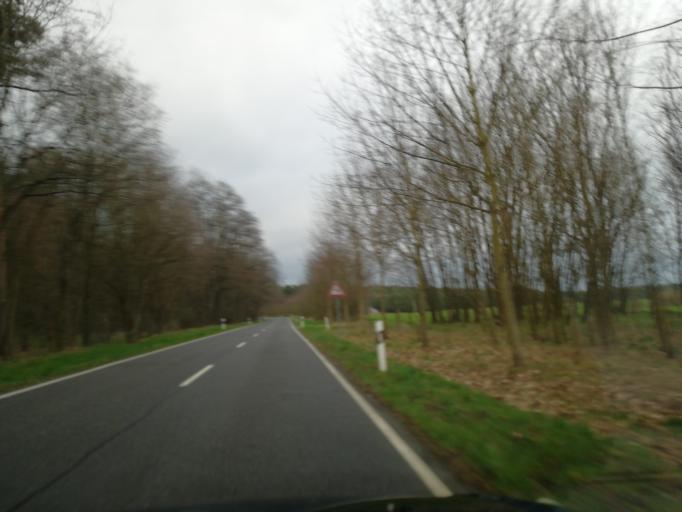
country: DE
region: Brandenburg
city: Vetschau
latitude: 51.7213
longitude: 14.0940
